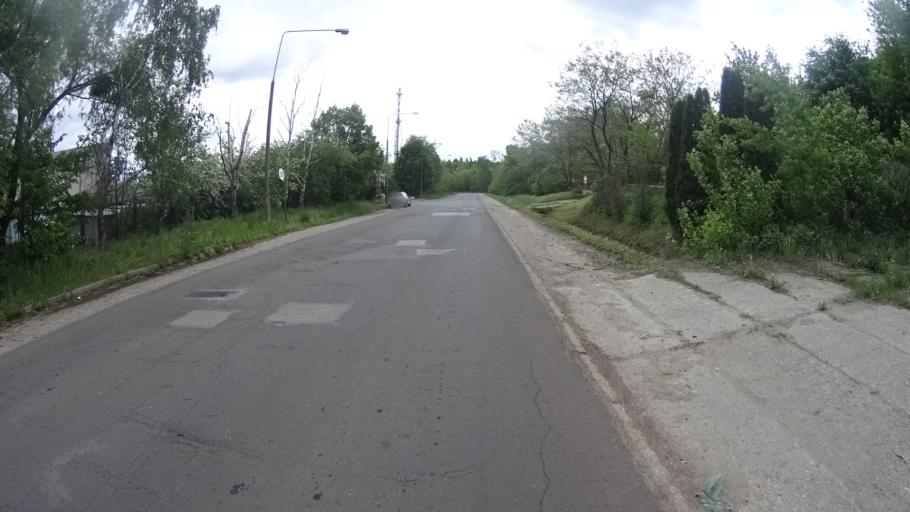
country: PL
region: Masovian Voivodeship
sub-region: Warszawa
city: Bemowo
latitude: 52.2796
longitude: 20.8811
